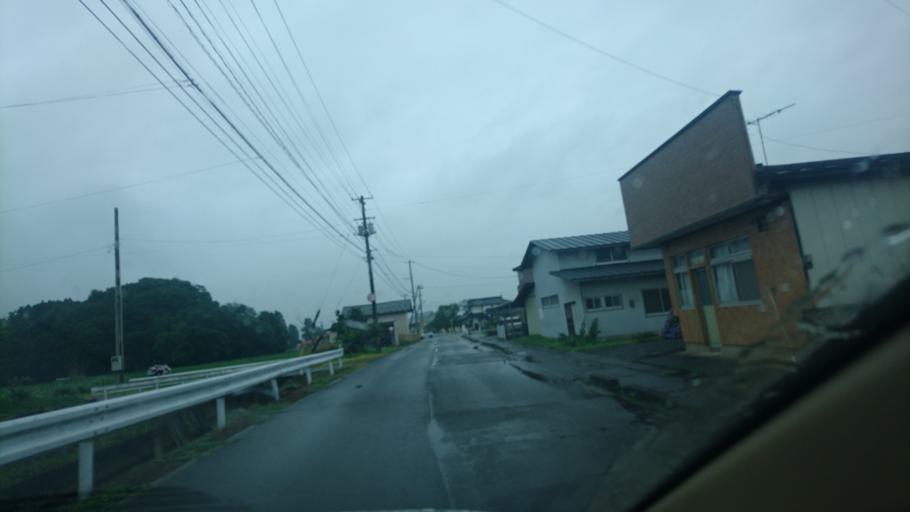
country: JP
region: Iwate
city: Kitakami
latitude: 39.2412
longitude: 141.1217
